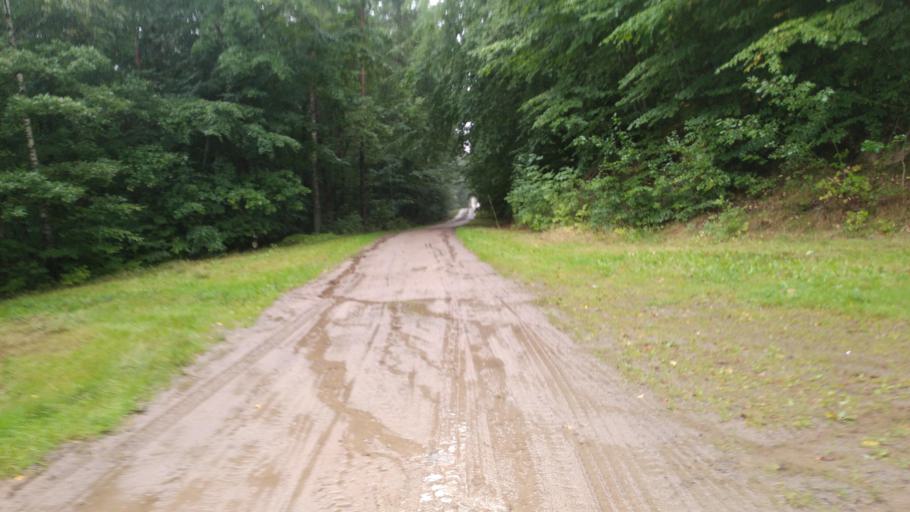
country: PL
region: Pomeranian Voivodeship
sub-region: Powiat wejherowski
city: Goscicino
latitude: 54.6272
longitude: 18.1408
